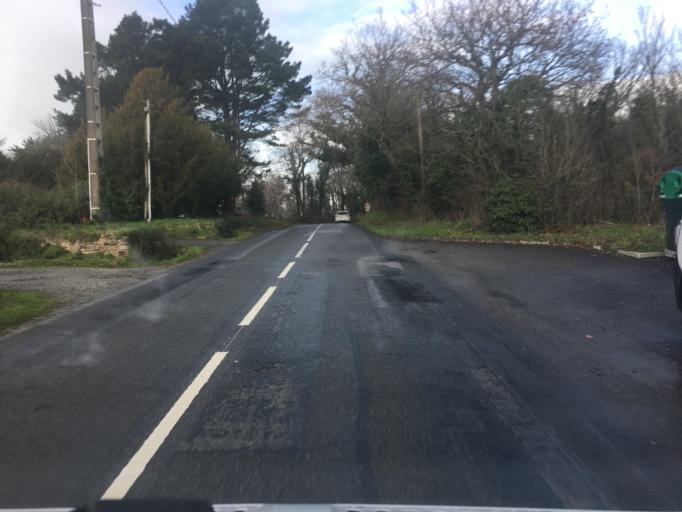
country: FR
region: Brittany
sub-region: Departement du Morbihan
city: Sarzeau
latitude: 47.5172
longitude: -2.7675
